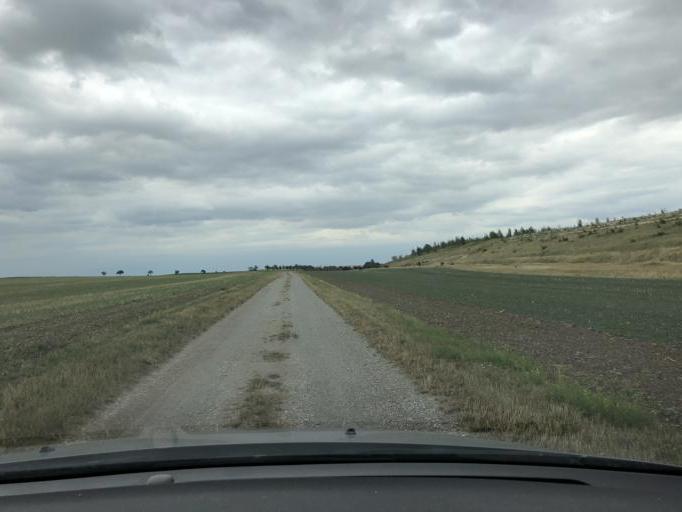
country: DE
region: Saxony-Anhalt
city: Nienburg/Saale
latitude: 51.8315
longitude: 11.7939
